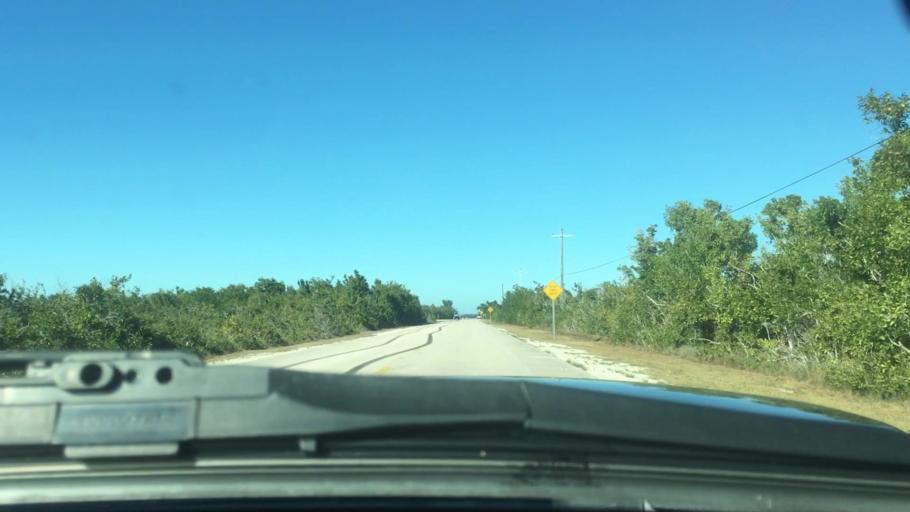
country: US
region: Florida
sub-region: Monroe County
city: Cudjoe Key
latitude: 24.6907
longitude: -81.4996
